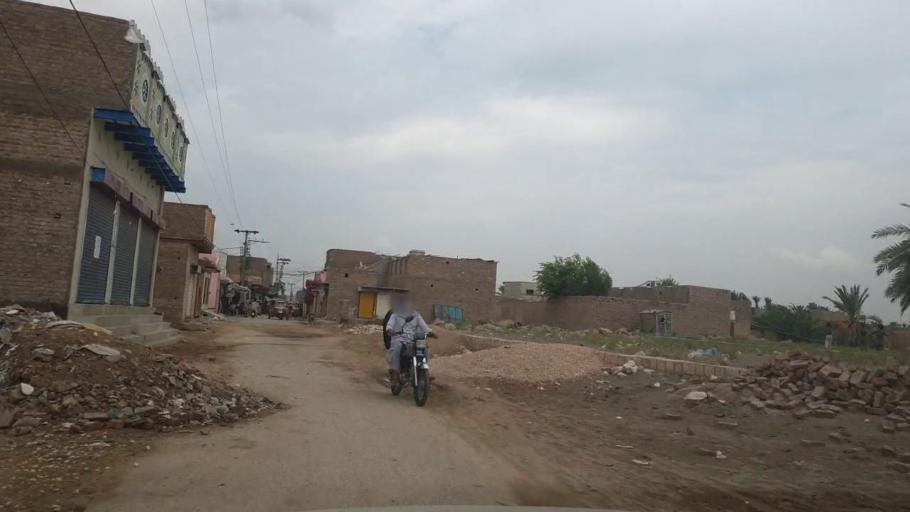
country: PK
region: Sindh
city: Khairpur
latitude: 27.5425
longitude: 68.7410
